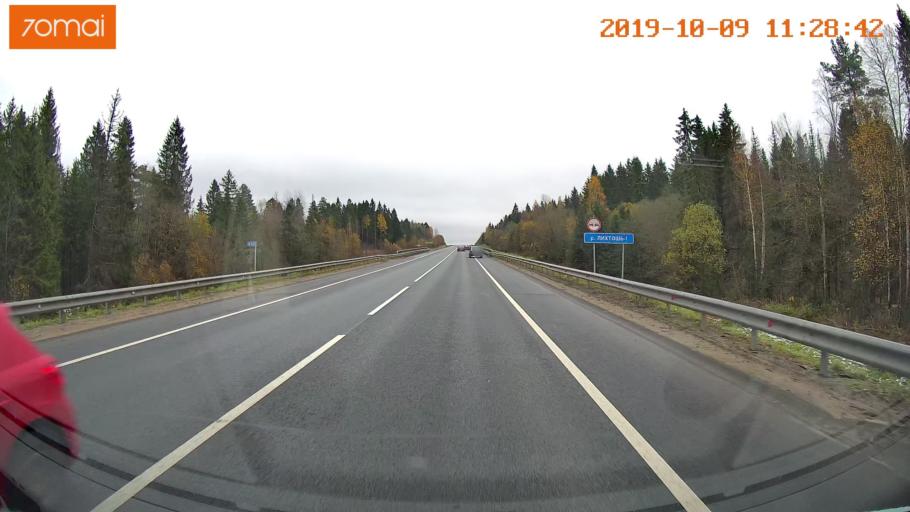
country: RU
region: Vologda
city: Vologda
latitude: 59.0664
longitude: 40.0425
